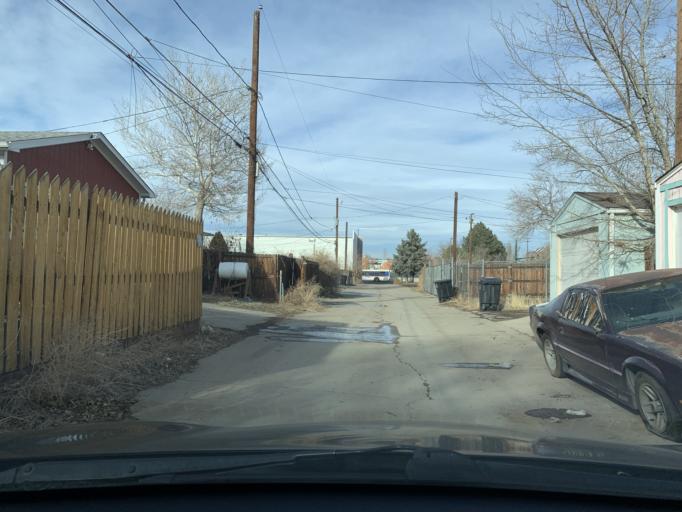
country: US
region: Colorado
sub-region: Jefferson County
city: Edgewater
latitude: 39.7394
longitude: -105.0304
